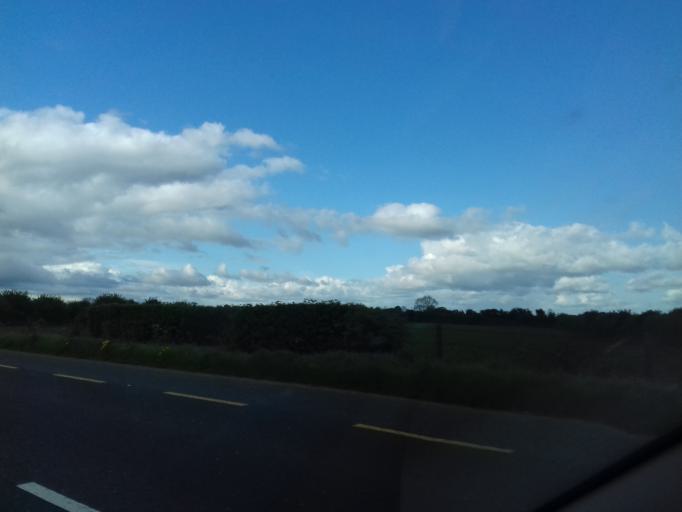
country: IE
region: Leinster
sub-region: Kilkenny
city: Kilkenny
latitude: 52.6067
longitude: -7.2430
